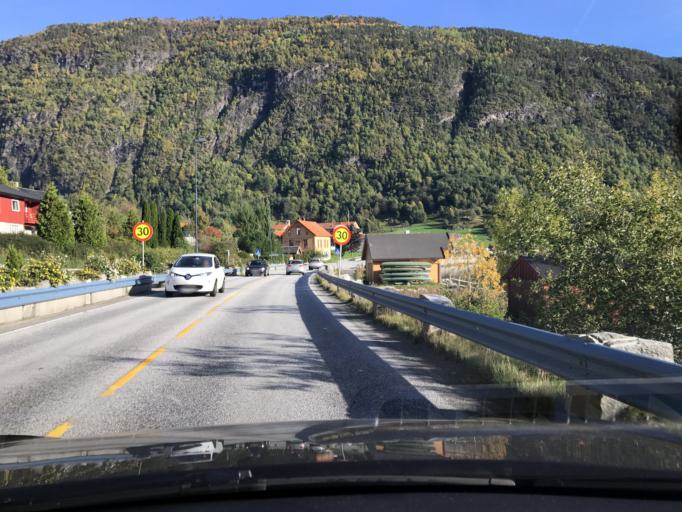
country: NO
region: Sogn og Fjordane
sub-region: Sogndal
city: Sogndalsfjora
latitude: 61.2322
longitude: 7.1133
